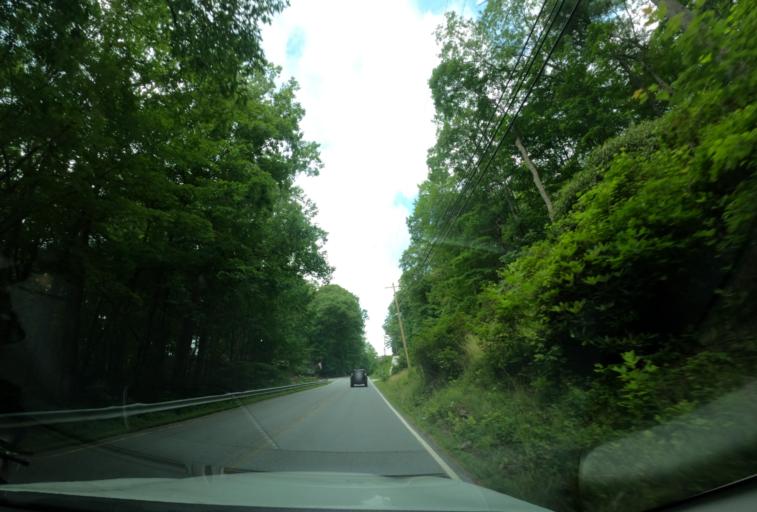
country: US
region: North Carolina
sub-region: Jackson County
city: Cullowhee
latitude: 35.1082
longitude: -83.1236
